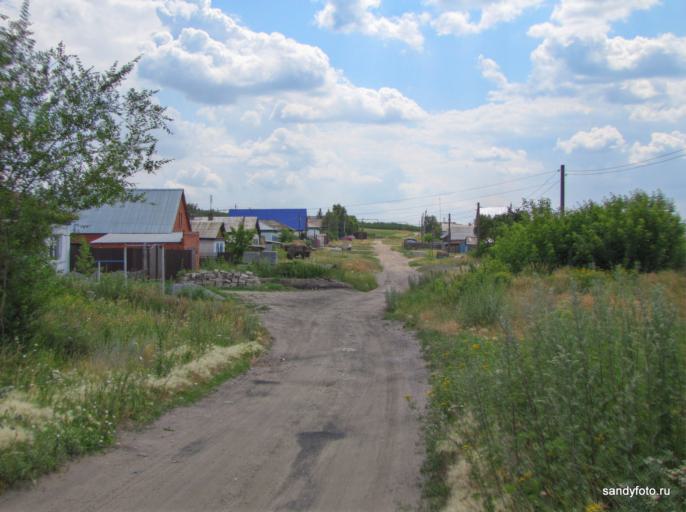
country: RU
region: Chelyabinsk
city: Troitsk
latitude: 54.0937
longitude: 61.5997
